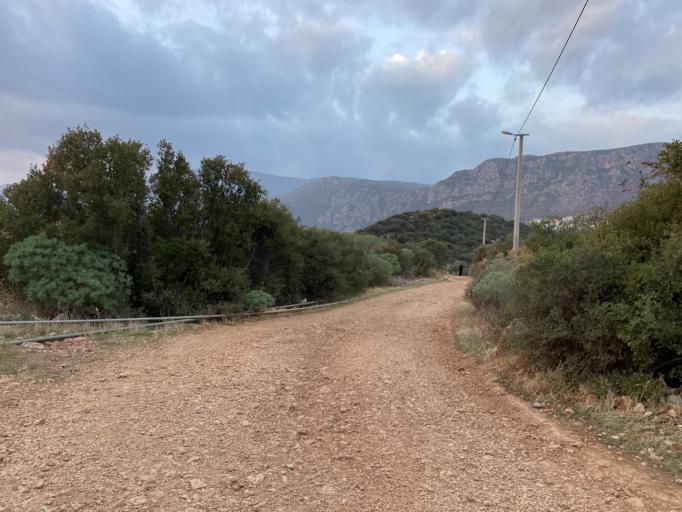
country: TR
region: Antalya
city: Kas
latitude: 36.1846
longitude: 29.6523
